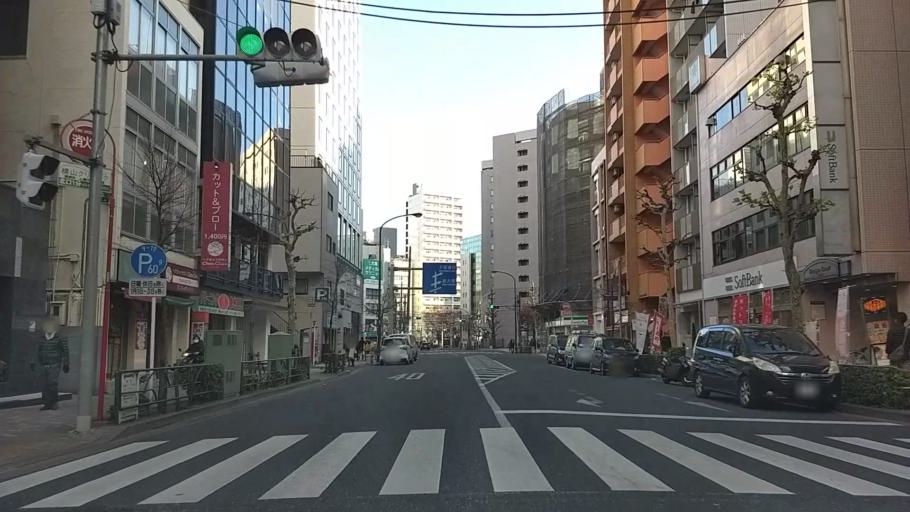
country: JP
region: Tokyo
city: Tokyo
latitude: 35.7336
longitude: 139.7283
